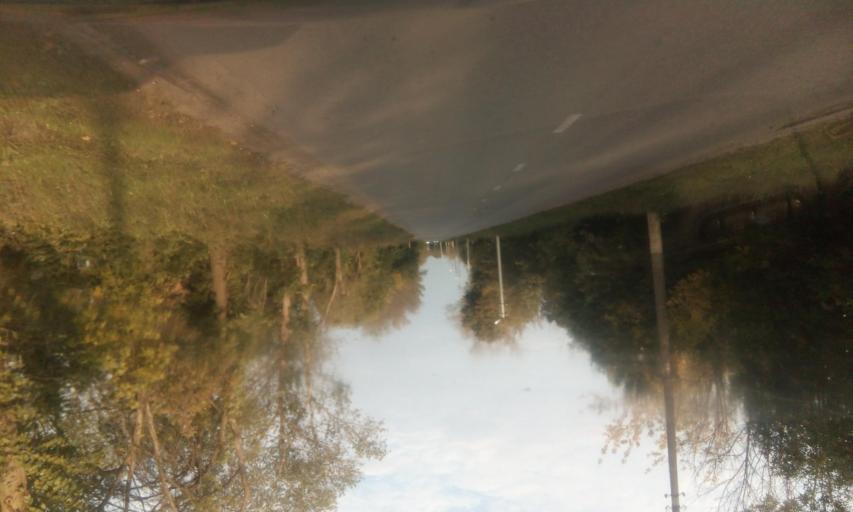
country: RU
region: Tula
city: Partizan
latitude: 53.9240
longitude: 38.1124
